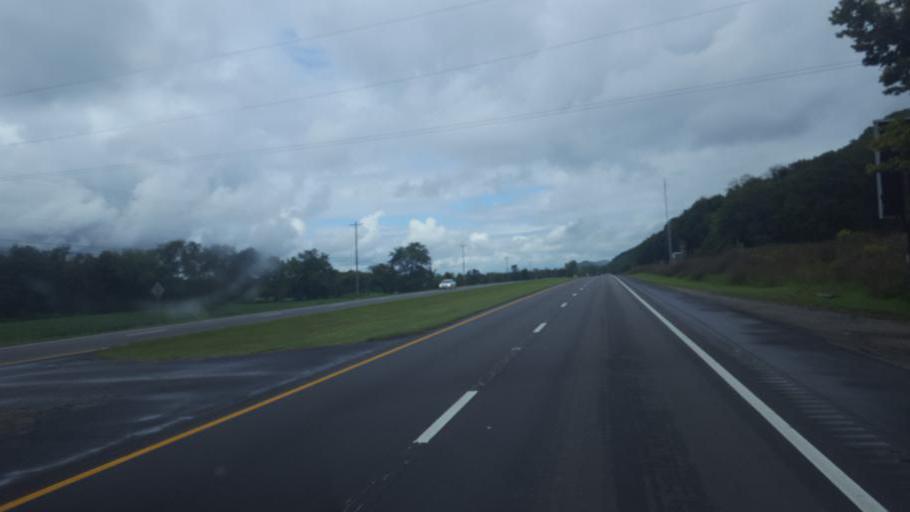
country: US
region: Ohio
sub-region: Scioto County
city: Rosemount
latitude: 38.8269
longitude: -82.9832
